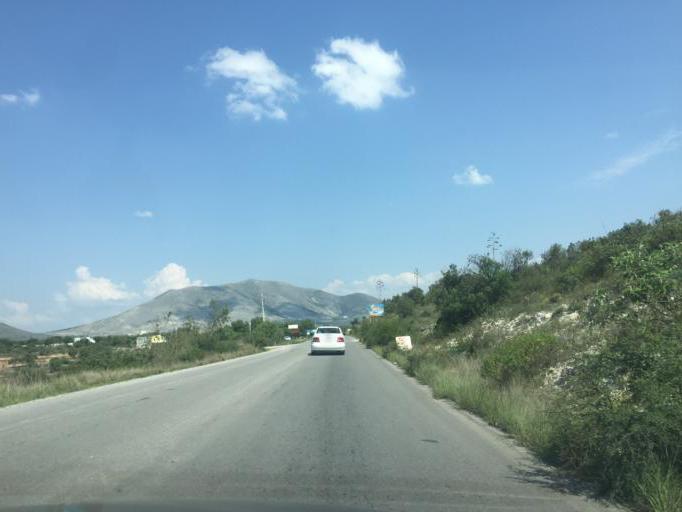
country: MX
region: Hidalgo
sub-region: Cardonal
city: Pozuelos
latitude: 20.6099
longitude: -99.1029
